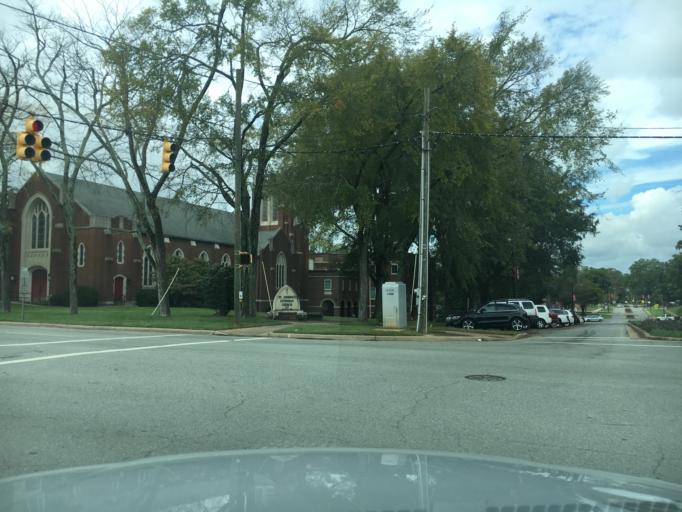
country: US
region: North Carolina
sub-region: Catawba County
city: Hickory
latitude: 35.7372
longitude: -81.3254
